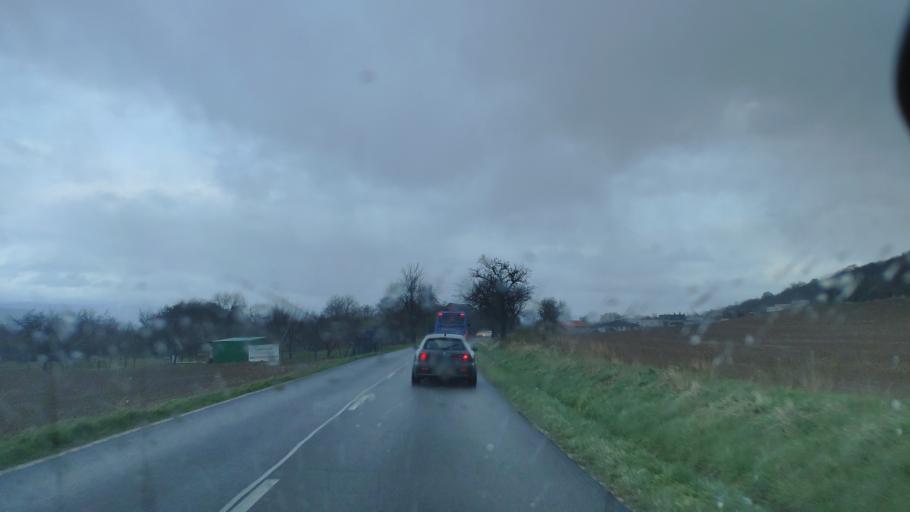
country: SK
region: Trenciansky
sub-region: Okres Nove Mesto nad Vahom
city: Nove Mesto nad Vahom
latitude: 48.7720
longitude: 17.8158
